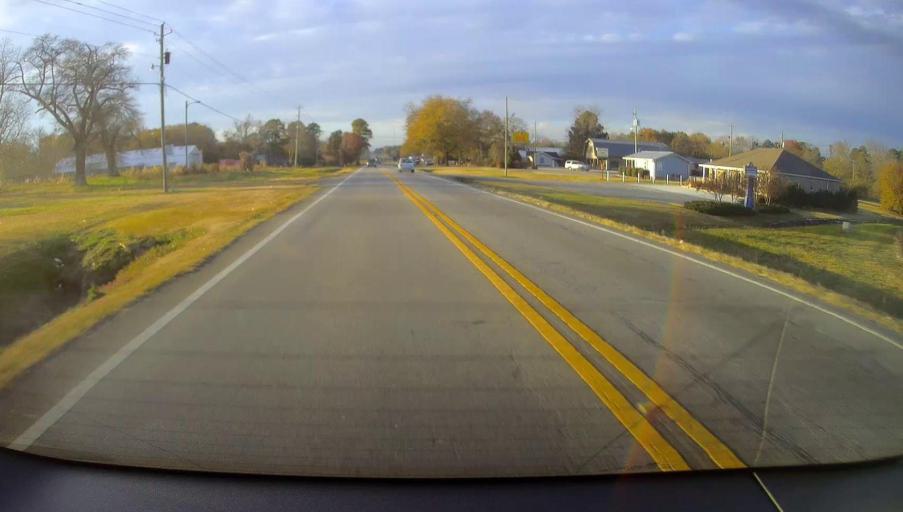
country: US
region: Alabama
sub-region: Blount County
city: Oneonta
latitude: 34.1095
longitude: -86.3794
